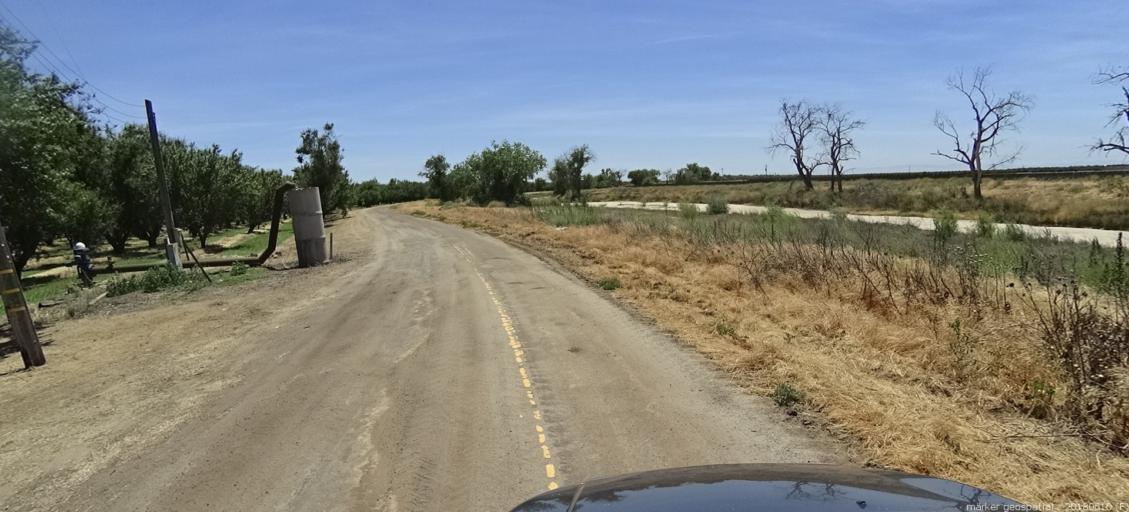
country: US
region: California
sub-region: Madera County
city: Chowchilla
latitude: 37.0686
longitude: -120.3977
